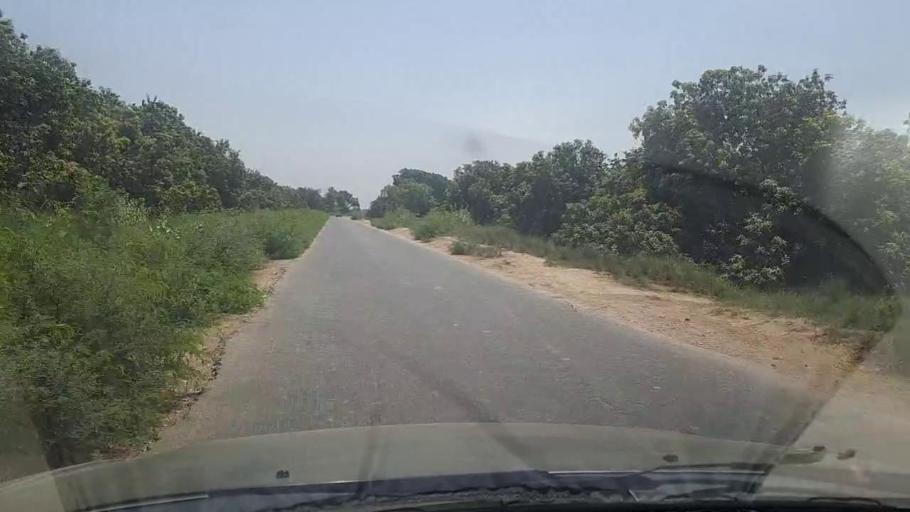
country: PK
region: Sindh
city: Tando Jam
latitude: 25.2848
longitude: 68.5984
